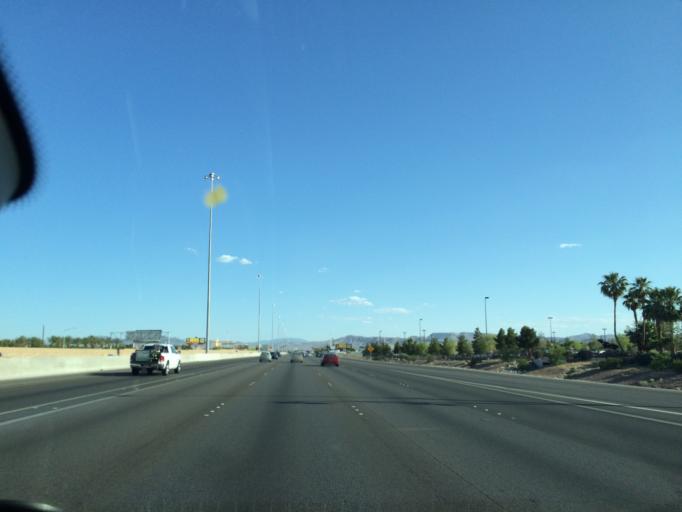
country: US
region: Nevada
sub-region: Clark County
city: Enterprise
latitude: 36.0414
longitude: -115.1809
